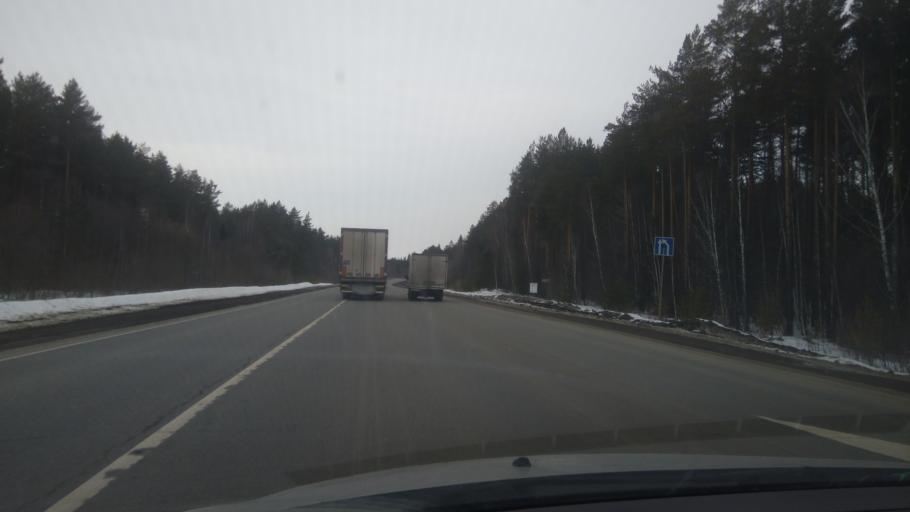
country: RU
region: Sverdlovsk
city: Ufimskiy
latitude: 56.7676
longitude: 58.1859
